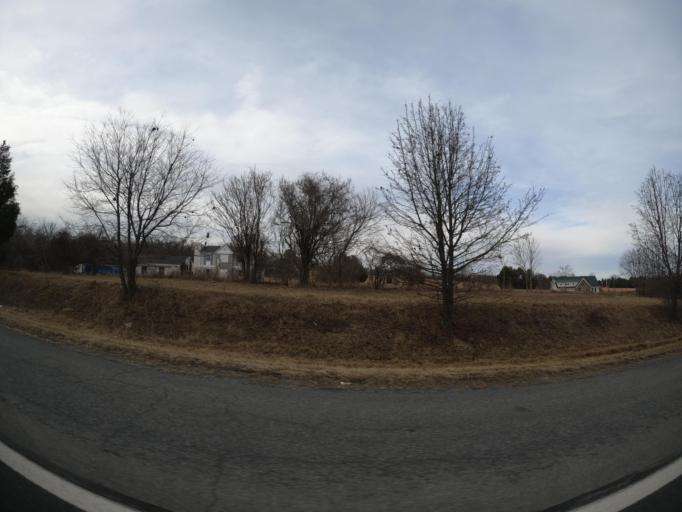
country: US
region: West Virginia
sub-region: Jefferson County
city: Bolivar
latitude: 39.3193
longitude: -77.7623
